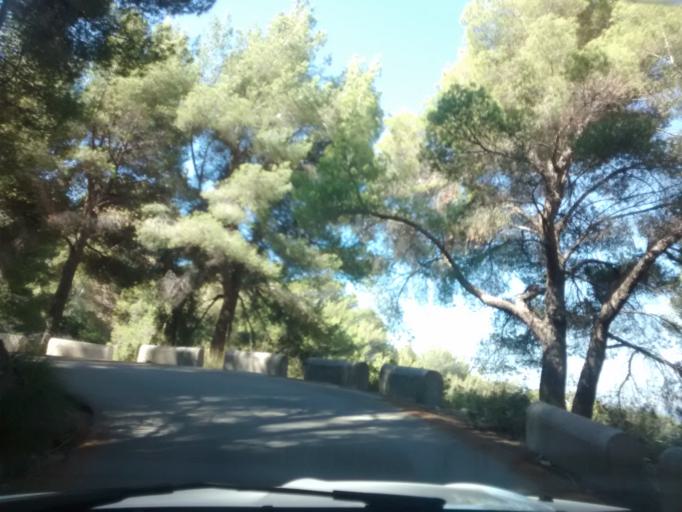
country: ES
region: Balearic Islands
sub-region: Illes Balears
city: Port d'Alcudia
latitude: 39.8782
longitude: 3.1753
